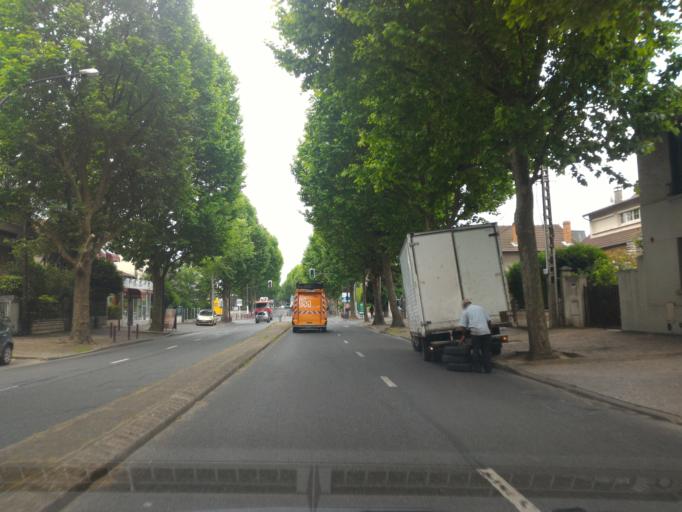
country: FR
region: Ile-de-France
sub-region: Departement du Val-de-Marne
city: L'Hay-les-Roses
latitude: 48.7773
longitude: 2.3403
